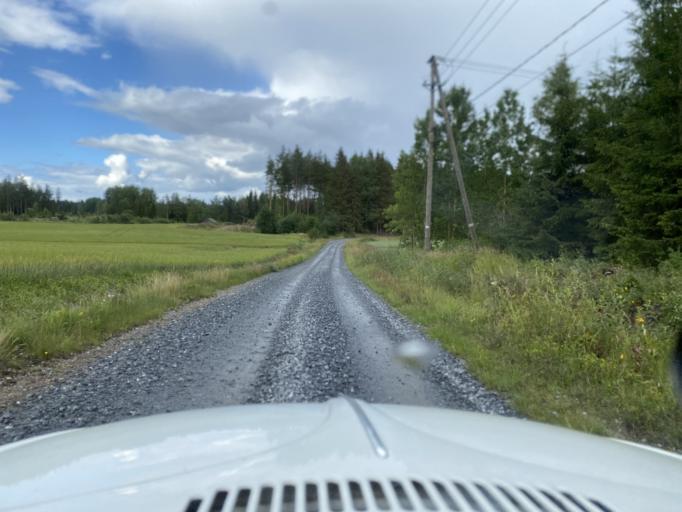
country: FI
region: Pirkanmaa
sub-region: Lounais-Pirkanmaa
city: Punkalaidun
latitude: 61.1286
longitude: 23.0648
